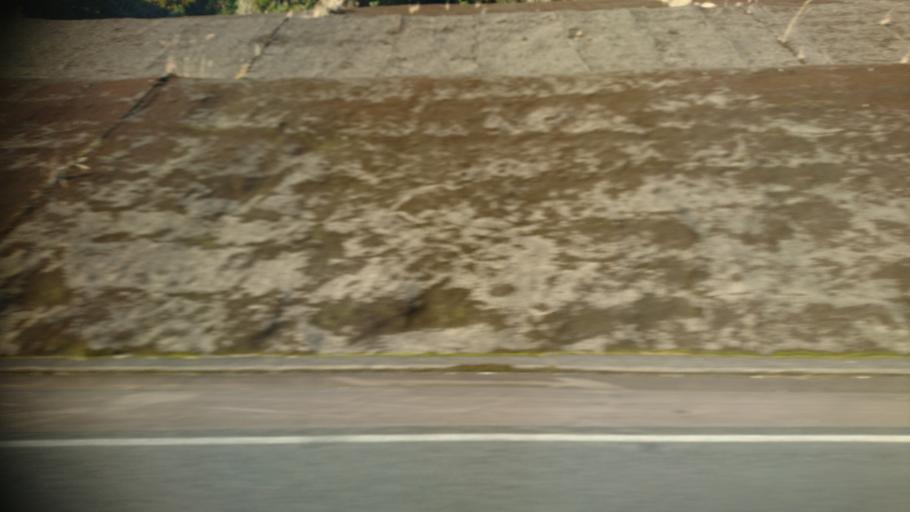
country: JP
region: Miyazaki
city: Miyakonojo
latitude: 31.7955
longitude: 131.1710
